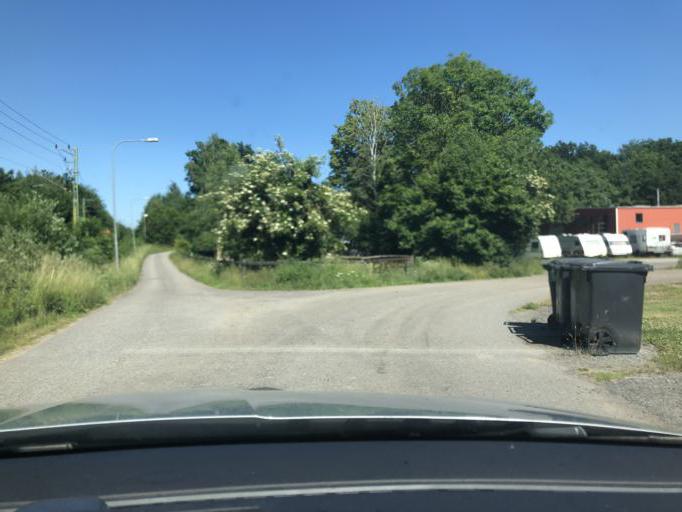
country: SE
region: Blekinge
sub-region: Karlshamns Kommun
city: Morrum
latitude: 56.1897
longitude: 14.6815
